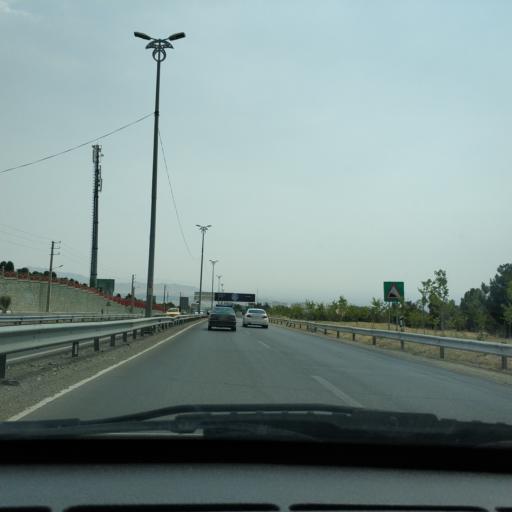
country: IR
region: Tehran
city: Tajrish
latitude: 35.7790
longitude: 51.5621
